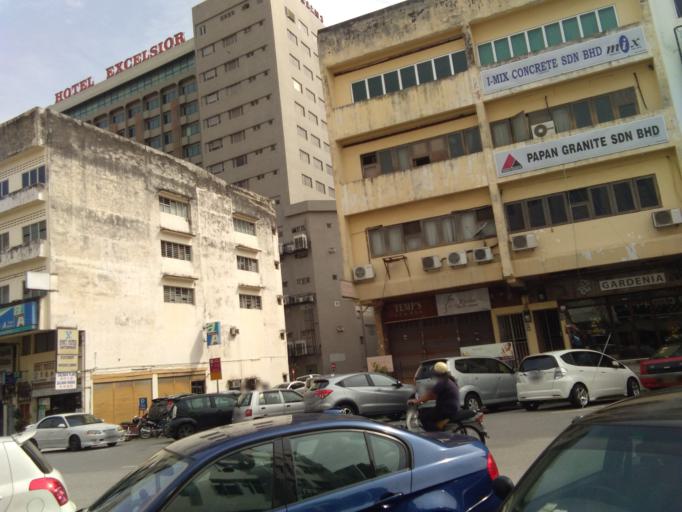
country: MY
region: Perak
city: Ipoh
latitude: 4.5967
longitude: 101.0870
